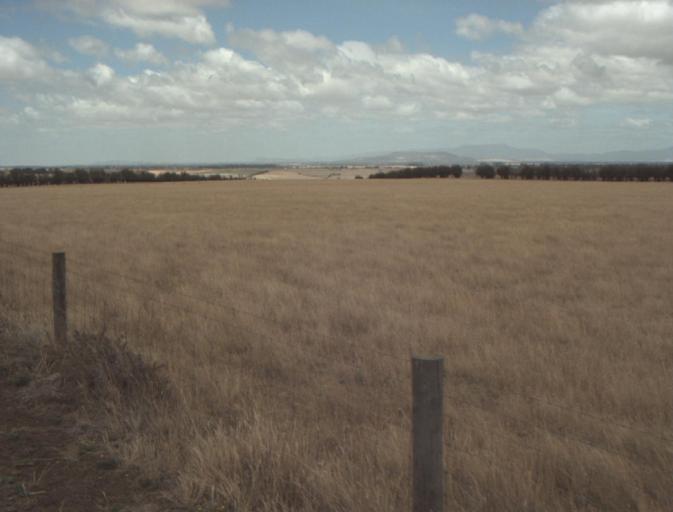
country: AU
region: Tasmania
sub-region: Northern Midlands
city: Evandale
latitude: -41.5270
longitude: 147.2717
